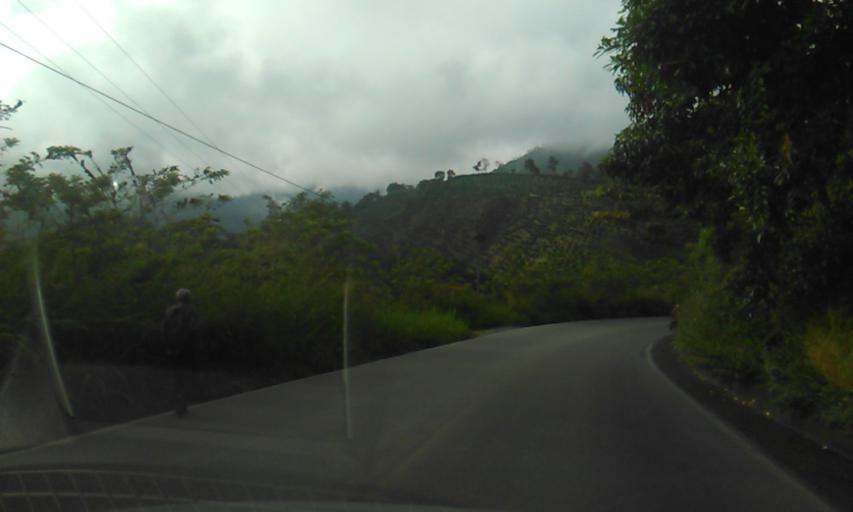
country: CO
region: Quindio
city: Cordoba
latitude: 4.4074
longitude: -75.7261
